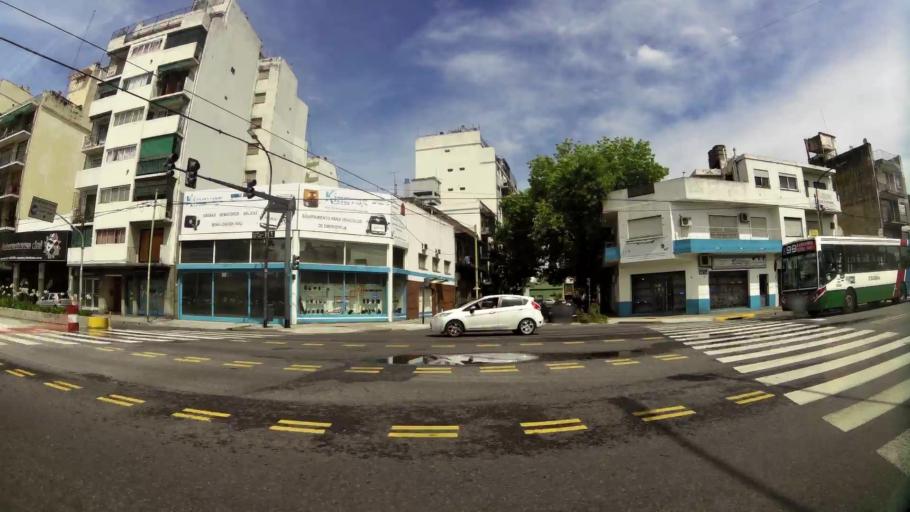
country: AR
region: Buenos Aires F.D.
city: Villa Santa Rita
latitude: -34.6276
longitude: -58.4920
